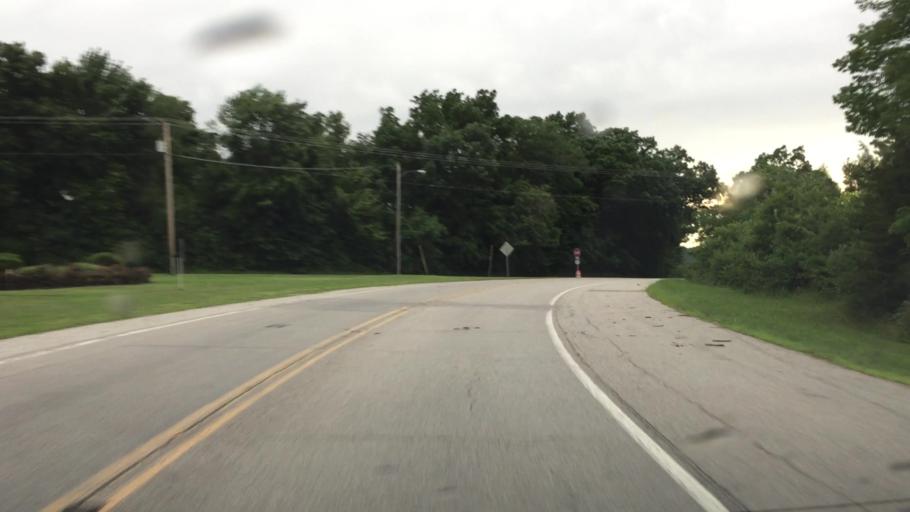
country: US
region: Illinois
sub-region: Hancock County
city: Hamilton
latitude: 40.3974
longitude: -91.3518
